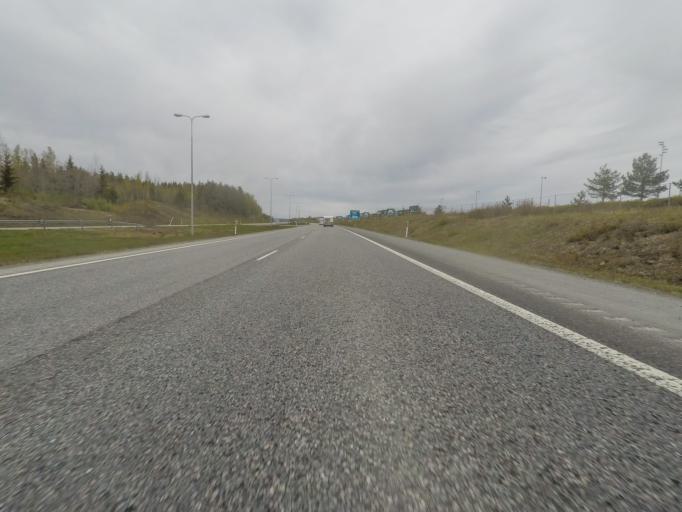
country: FI
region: Pirkanmaa
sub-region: Tampere
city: Lempaeaelae
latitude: 61.3575
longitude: 23.7921
